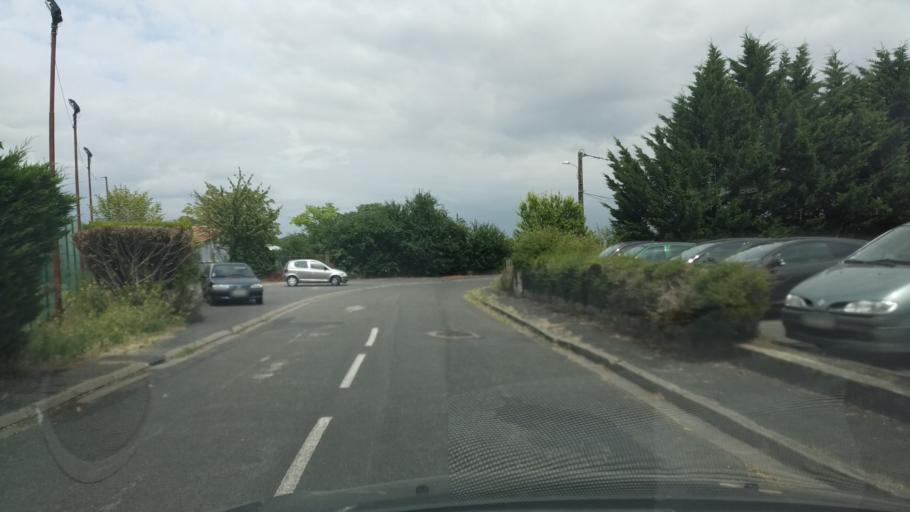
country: FR
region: Poitou-Charentes
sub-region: Departement de la Vienne
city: Saint-Maurice-la-Clouere
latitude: 46.3714
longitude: 0.4067
